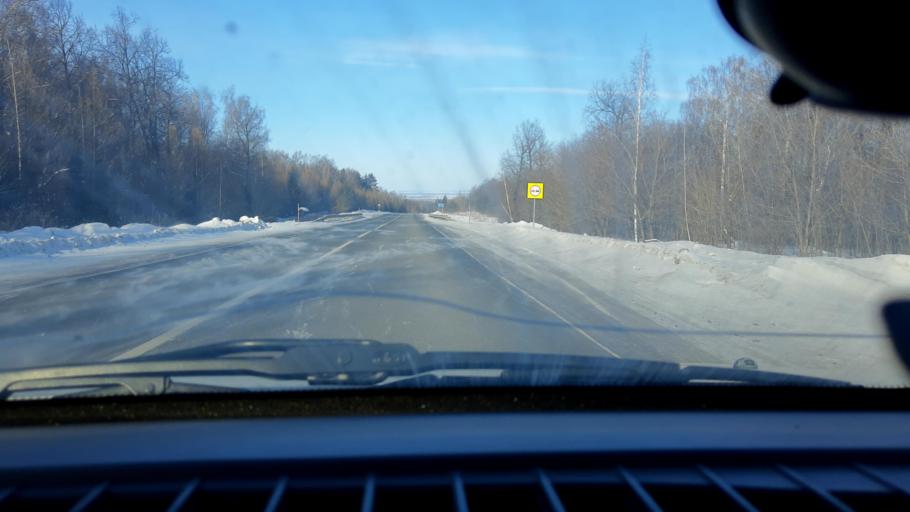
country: RU
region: Bashkortostan
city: Avdon
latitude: 54.8424
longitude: 55.7134
